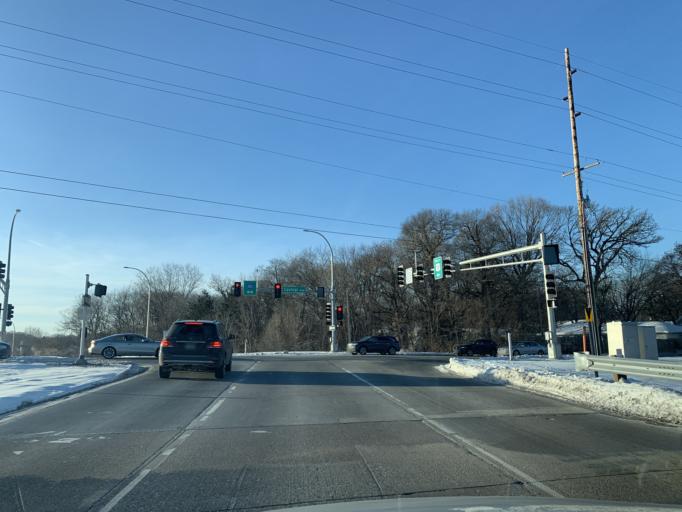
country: US
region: Minnesota
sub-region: Hennepin County
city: Wayzata
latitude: 44.9767
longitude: -93.5016
